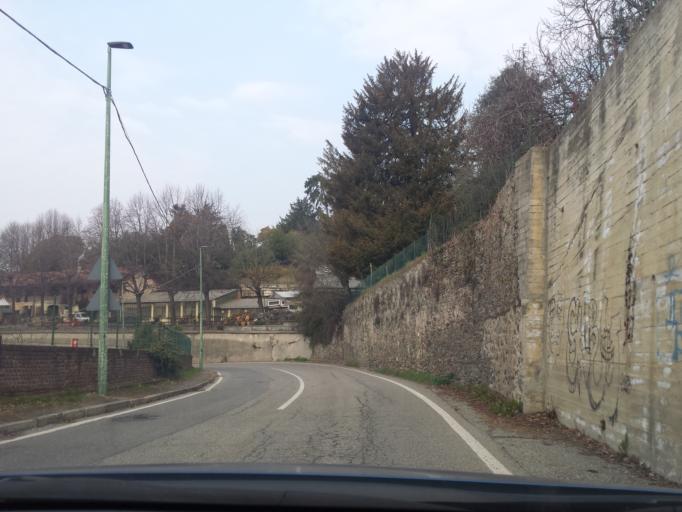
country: IT
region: Piedmont
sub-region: Provincia di Torino
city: Turin
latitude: 45.0565
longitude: 7.7130
